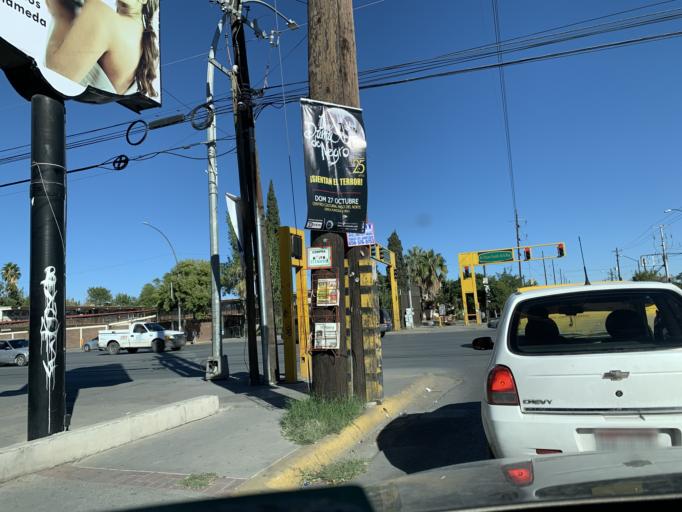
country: MX
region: Chihuahua
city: Ciudad Juarez
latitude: 31.7374
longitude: -106.4408
